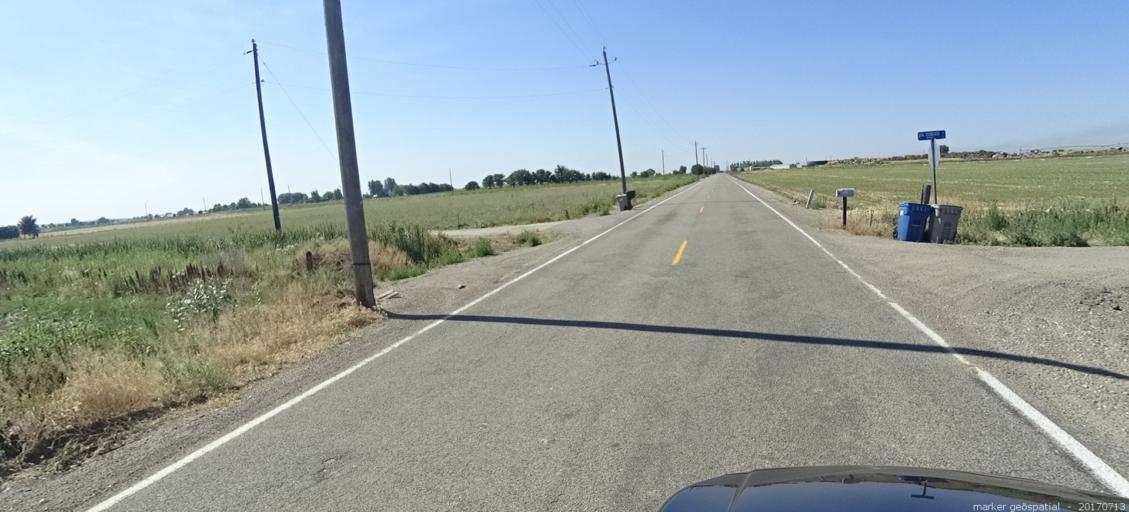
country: US
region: Idaho
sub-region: Ada County
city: Kuna
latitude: 43.5393
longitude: -116.3743
